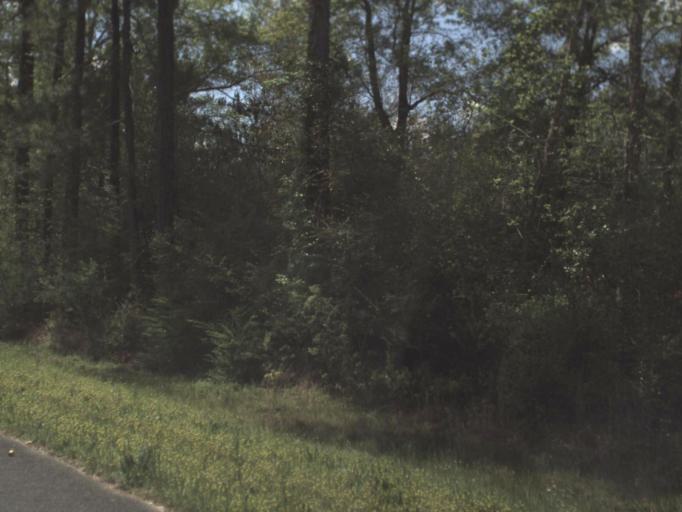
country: US
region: Florida
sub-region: Okaloosa County
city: Crestview
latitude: 30.8622
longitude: -86.6722
